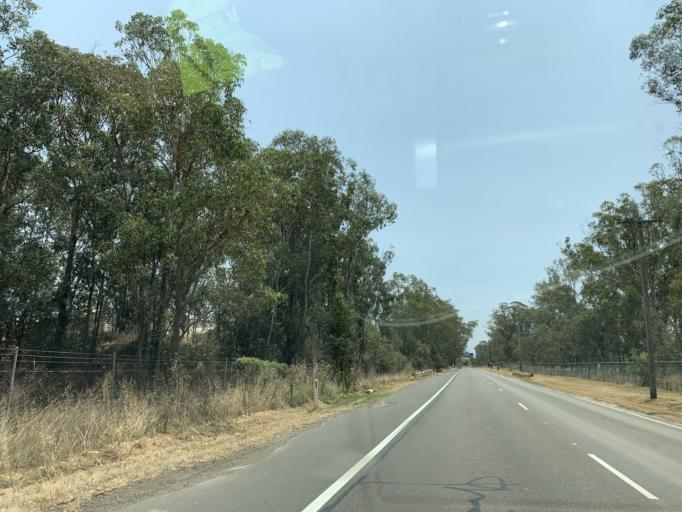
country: AU
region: New South Wales
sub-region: Fairfield
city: Horsley Park
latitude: -33.8271
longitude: 150.8720
